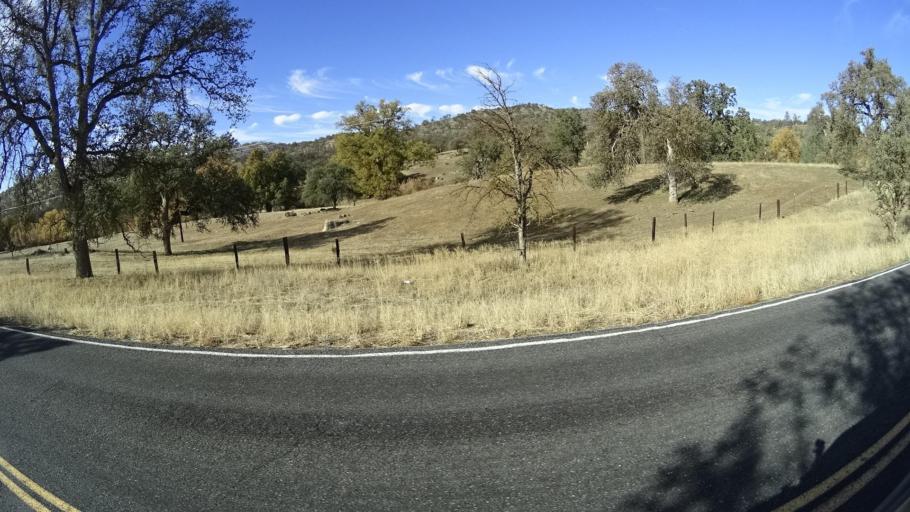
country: US
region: California
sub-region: Kern County
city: Alta Sierra
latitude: 35.6831
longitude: -118.7318
